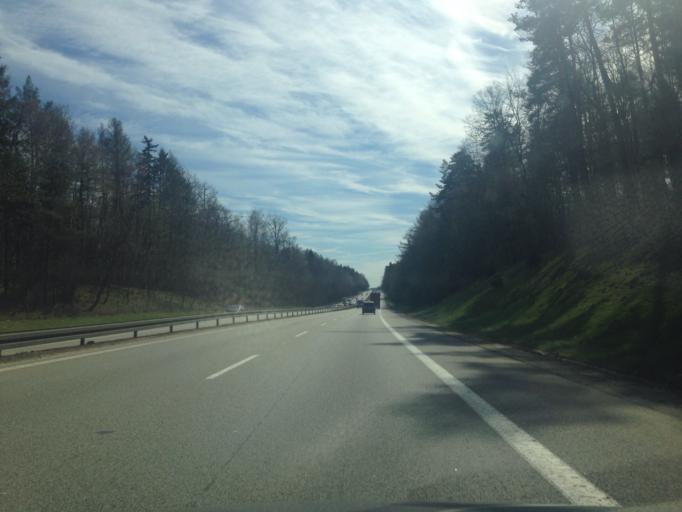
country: PL
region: Pomeranian Voivodeship
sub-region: Gdynia
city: Wielki Kack
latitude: 54.4491
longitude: 18.4925
